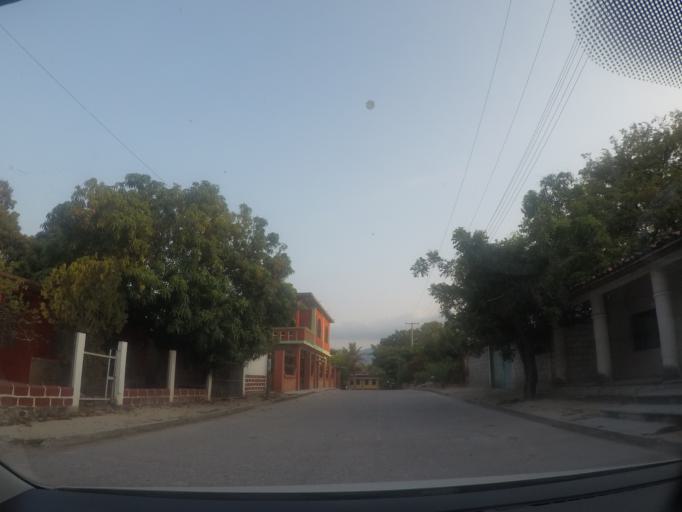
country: MX
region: Oaxaca
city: San Pedro Comitancillo
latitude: 16.5835
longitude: -95.2079
